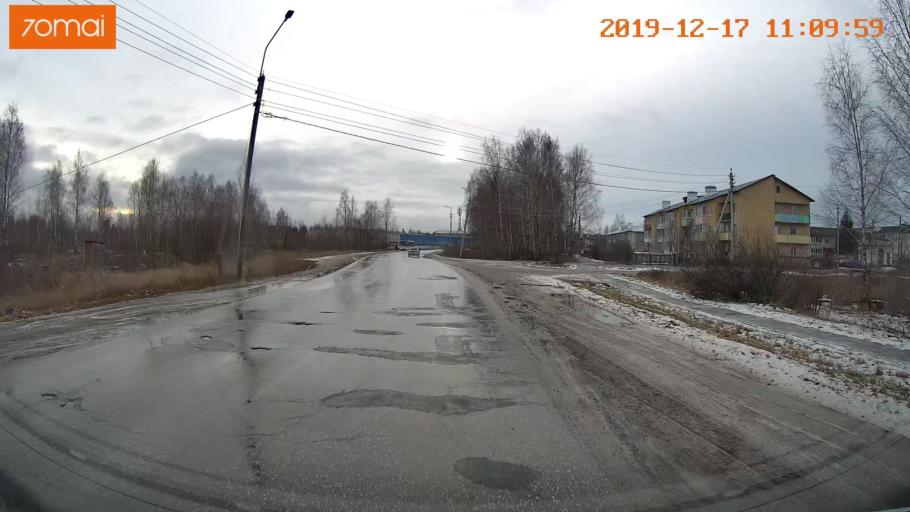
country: RU
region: Vladimir
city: Gus'-Khrustal'nyy
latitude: 55.5963
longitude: 40.6414
